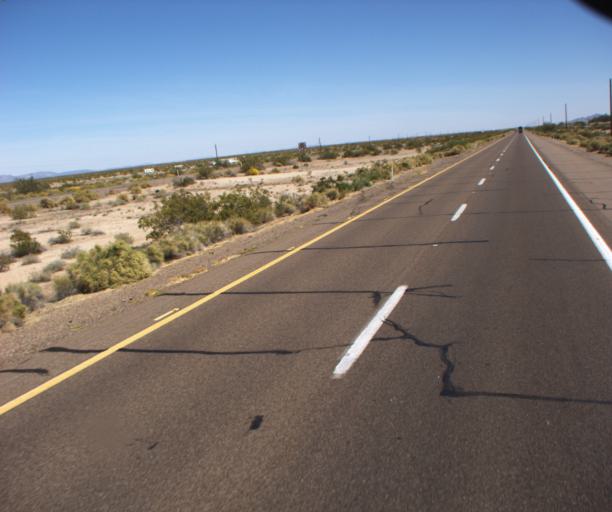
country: US
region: Arizona
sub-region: Yuma County
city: Wellton
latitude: 32.7382
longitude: -113.6939
